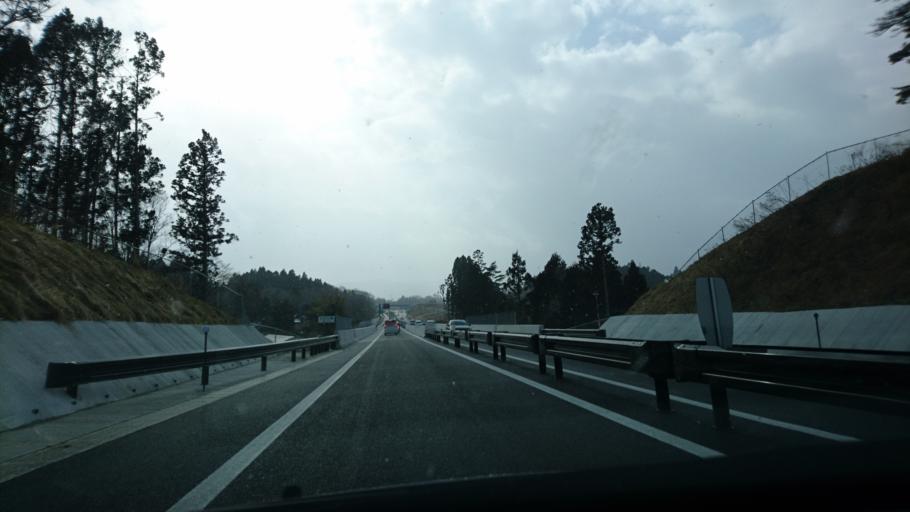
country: JP
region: Iwate
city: Ofunato
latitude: 38.7958
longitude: 141.5262
